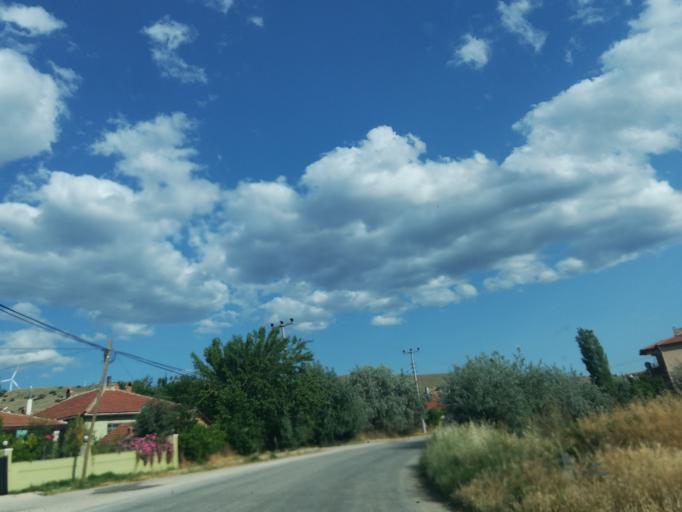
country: TR
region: Afyonkarahisar
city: Dinar
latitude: 38.0821
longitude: 30.1669
